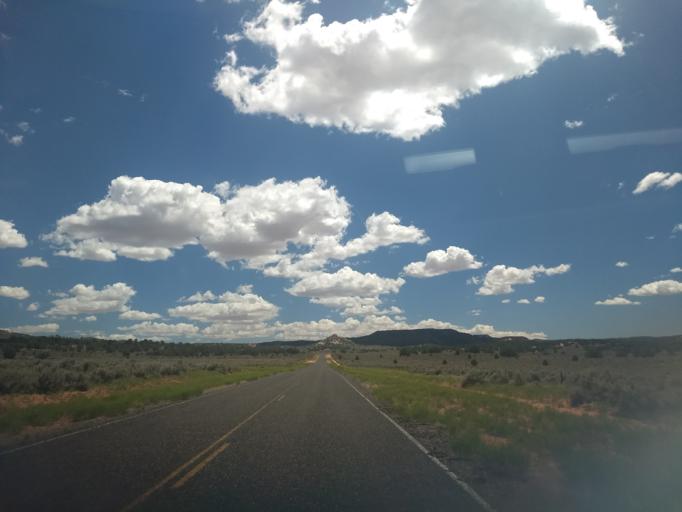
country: US
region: Utah
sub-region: Kane County
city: Kanab
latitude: 37.1561
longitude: -112.6692
